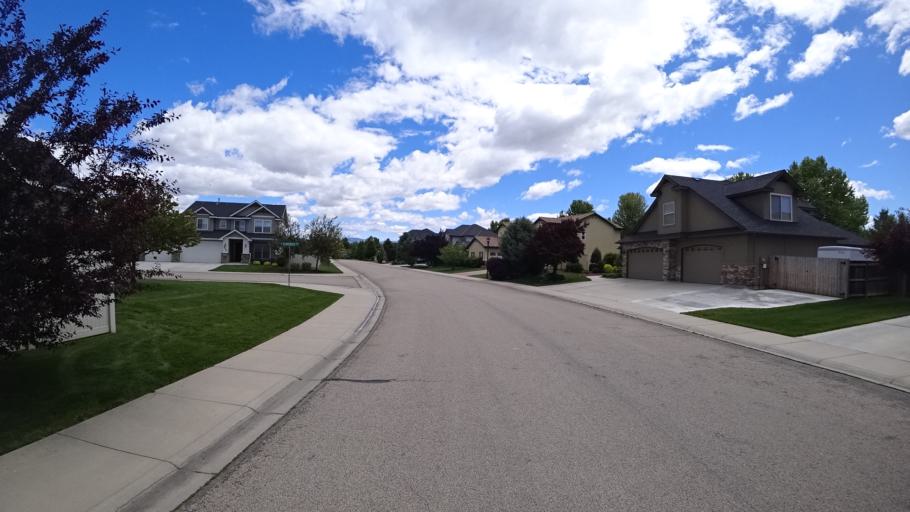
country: US
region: Idaho
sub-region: Ada County
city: Eagle
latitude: 43.6544
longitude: -116.3423
